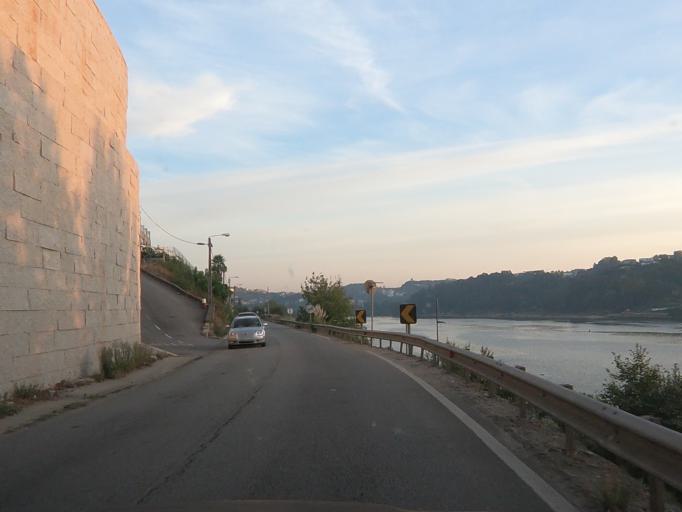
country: PT
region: Porto
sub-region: Gondomar
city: Valbom
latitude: 41.1367
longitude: -8.5710
